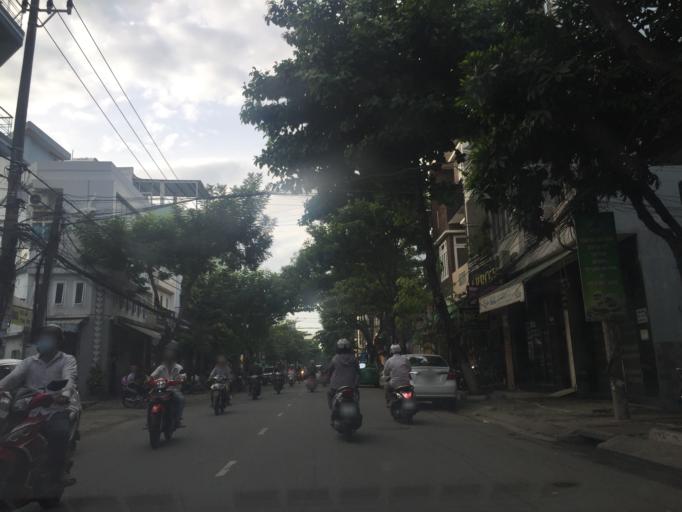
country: VN
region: Da Nang
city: Da Nang
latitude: 16.0772
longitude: 108.2121
